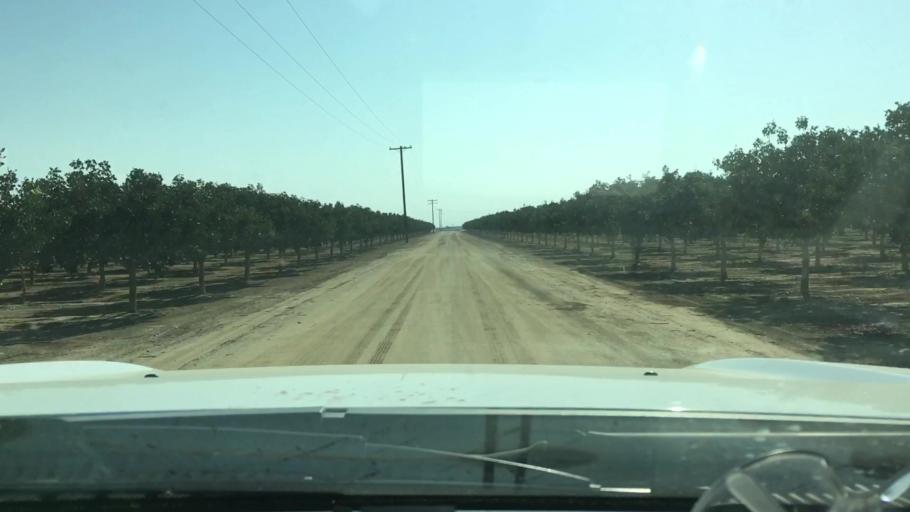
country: US
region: California
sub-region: Kern County
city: Lost Hills
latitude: 35.6302
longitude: -119.5845
